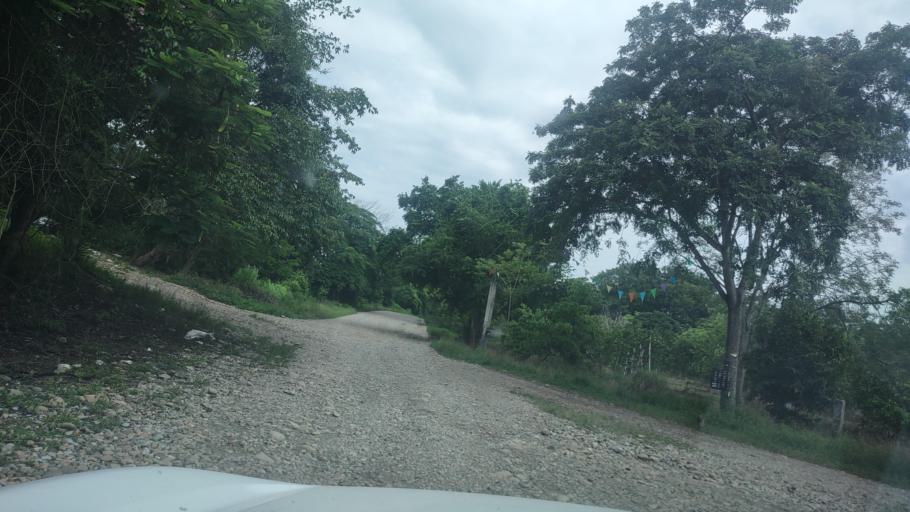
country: MX
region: Veracruz
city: Tepetzintla
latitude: 21.0493
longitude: -97.9971
